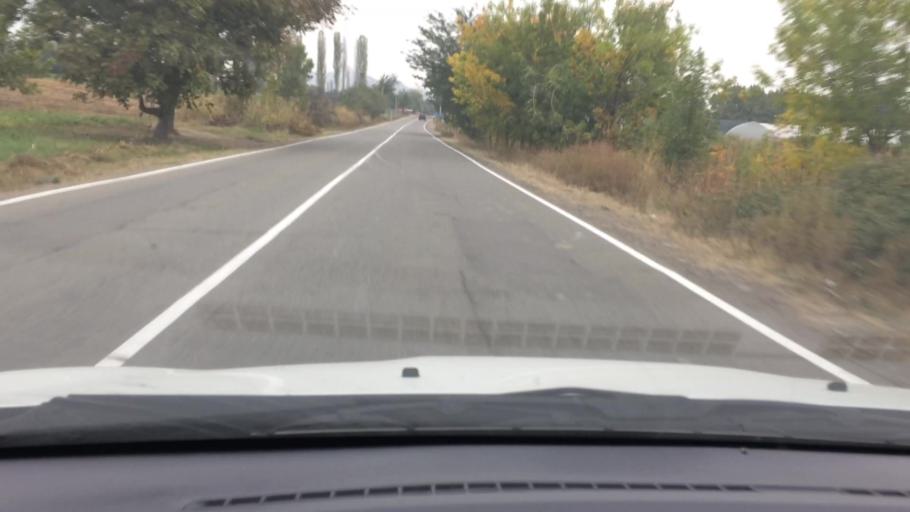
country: GE
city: Naghvarevi
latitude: 41.3186
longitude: 44.7950
